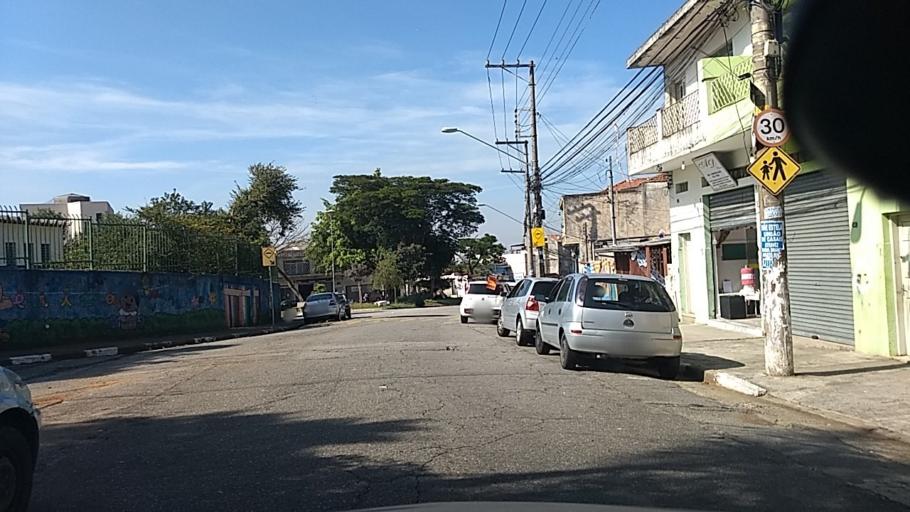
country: BR
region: Sao Paulo
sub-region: Guarulhos
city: Guarulhos
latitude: -23.5000
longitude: -46.5754
